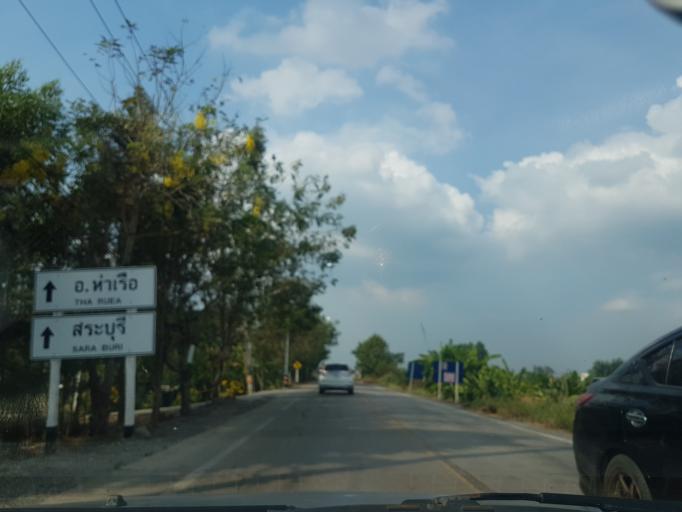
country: TH
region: Phra Nakhon Si Ayutthaya
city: Phachi
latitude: 14.4190
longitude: 100.7815
